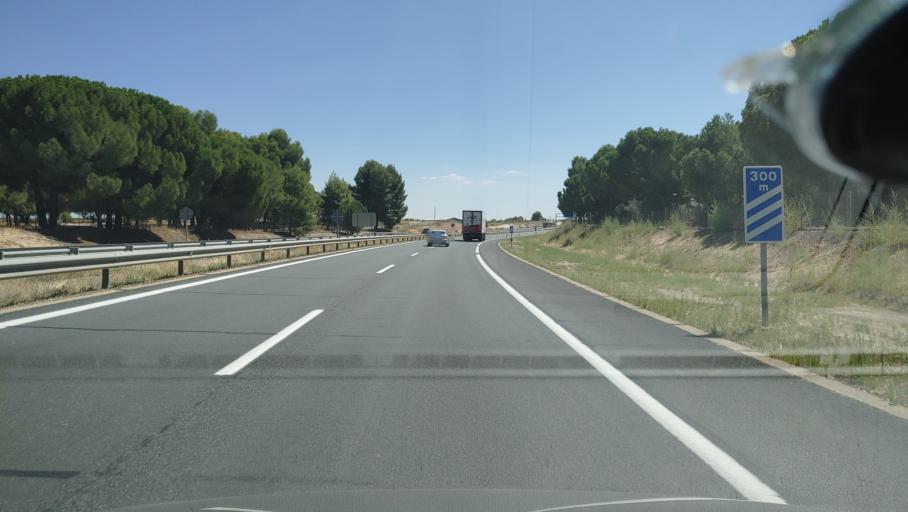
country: ES
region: Castille-La Mancha
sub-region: Provincia de Ciudad Real
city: Villarta de San Juan
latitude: 39.2424
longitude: -3.4144
